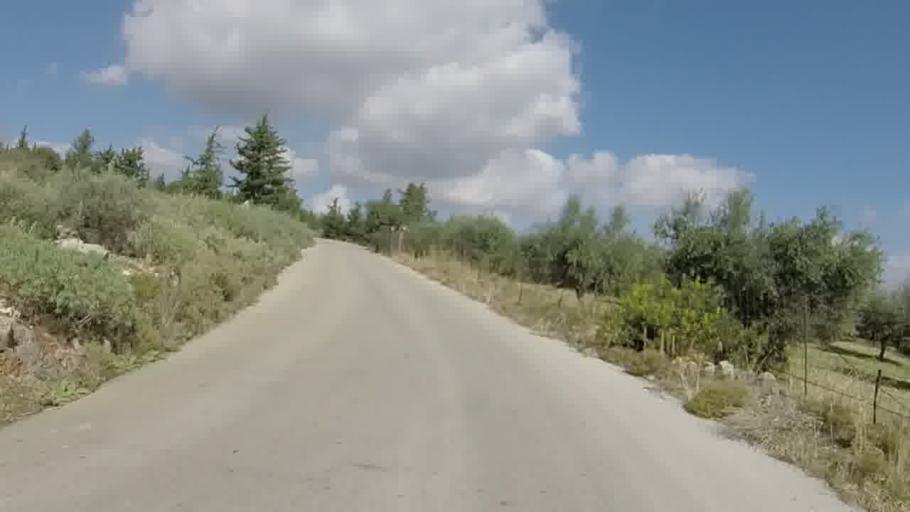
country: GR
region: Crete
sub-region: Nomos Chanias
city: Kalivai
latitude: 35.3894
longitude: 24.1318
